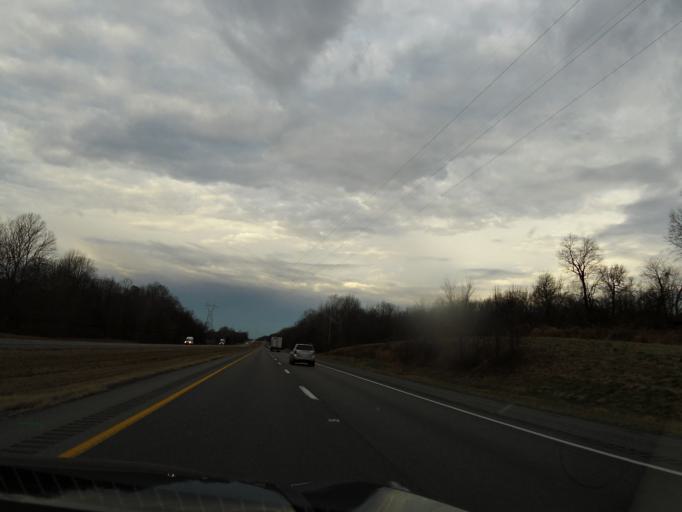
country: US
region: Kentucky
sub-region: Marshall County
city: Calvert City
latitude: 36.9919
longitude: -88.4053
